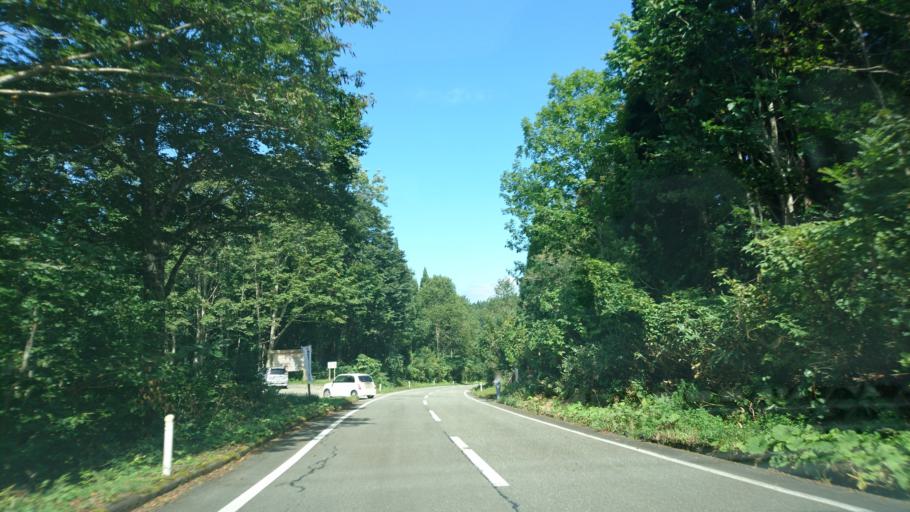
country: JP
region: Akita
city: Yuzawa
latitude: 38.9630
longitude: 140.7138
